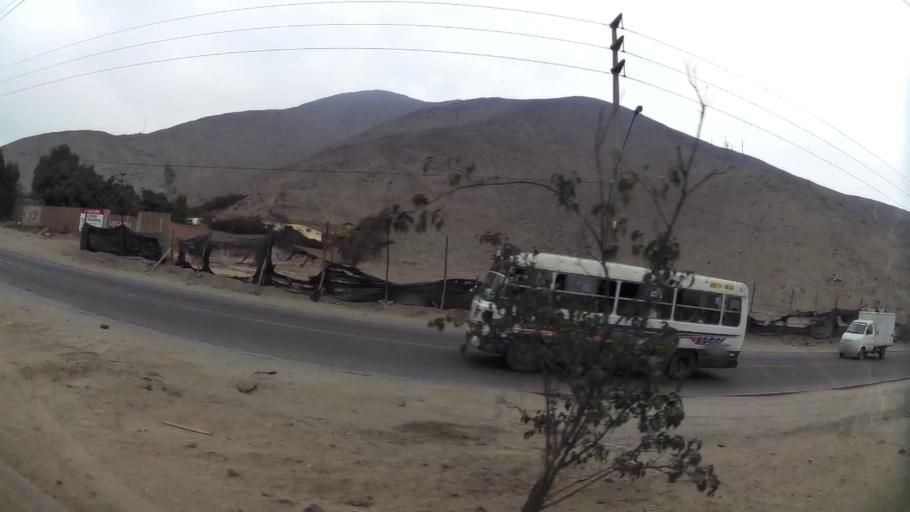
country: PE
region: Lima
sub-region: Lima
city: La Molina
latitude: -12.0859
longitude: -76.9137
